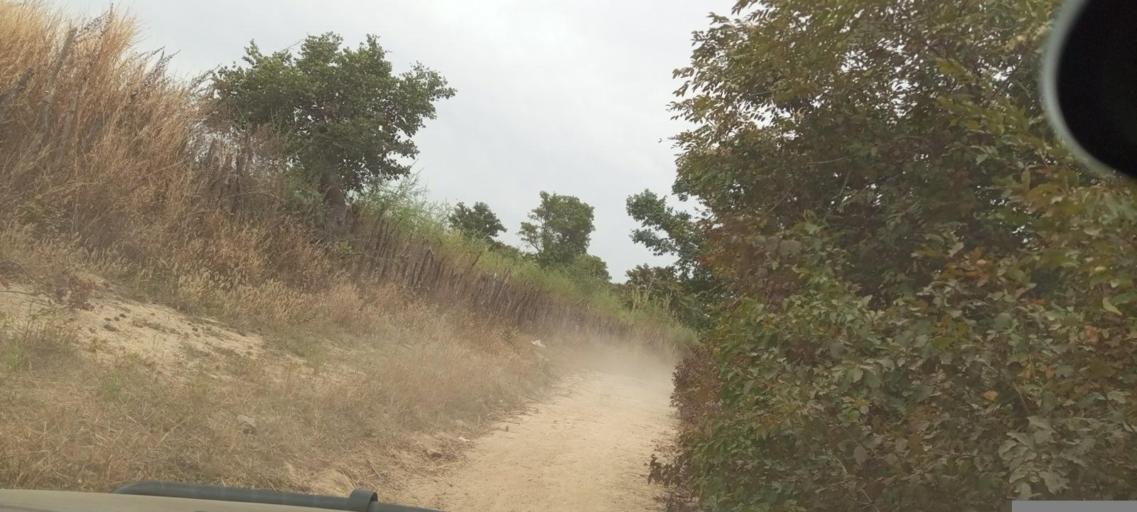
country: ML
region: Koulikoro
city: Kati
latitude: 12.7447
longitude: -8.3326
